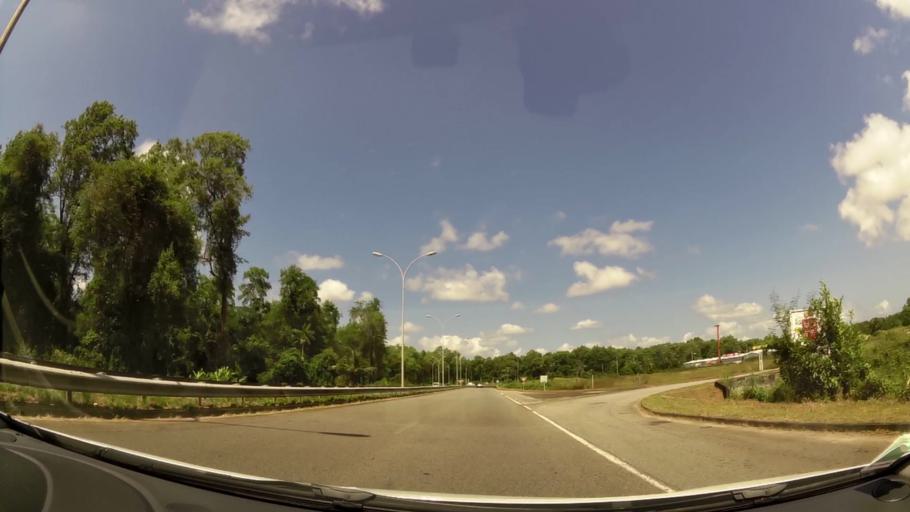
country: GF
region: Guyane
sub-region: Guyane
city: Cayenne
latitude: 4.9222
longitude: -52.3277
